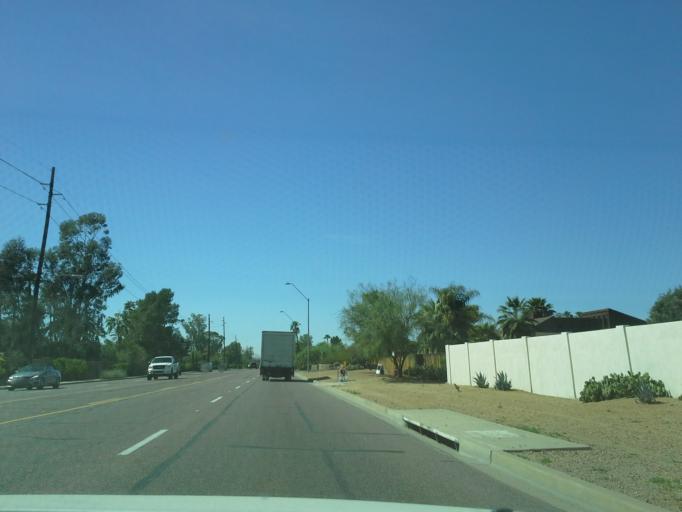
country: US
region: Arizona
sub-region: Maricopa County
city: Paradise Valley
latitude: 33.5969
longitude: -111.9458
